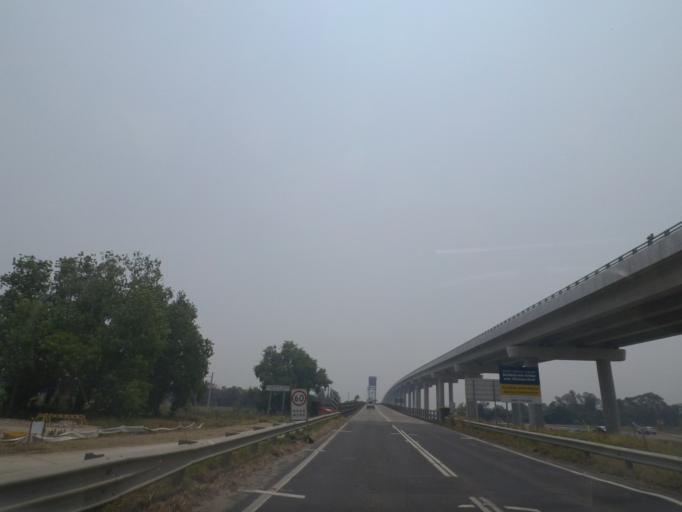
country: AU
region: New South Wales
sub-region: Clarence Valley
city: Maclean
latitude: -29.4348
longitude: 153.2406
